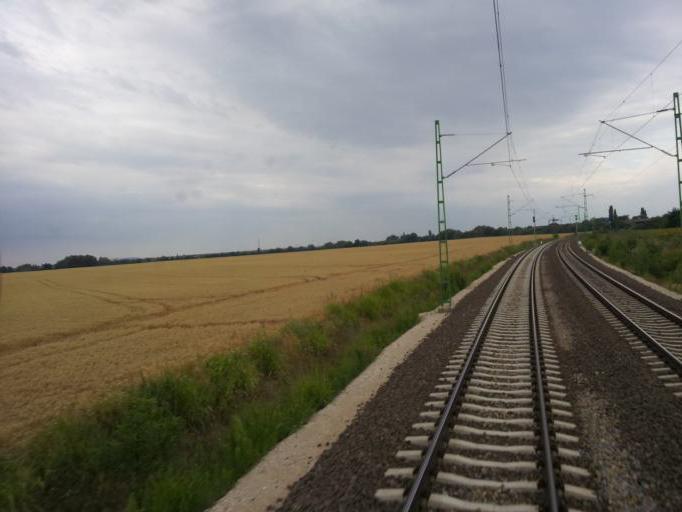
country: HU
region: Fejer
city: Szekesfehervar
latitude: 47.1699
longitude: 18.4749
